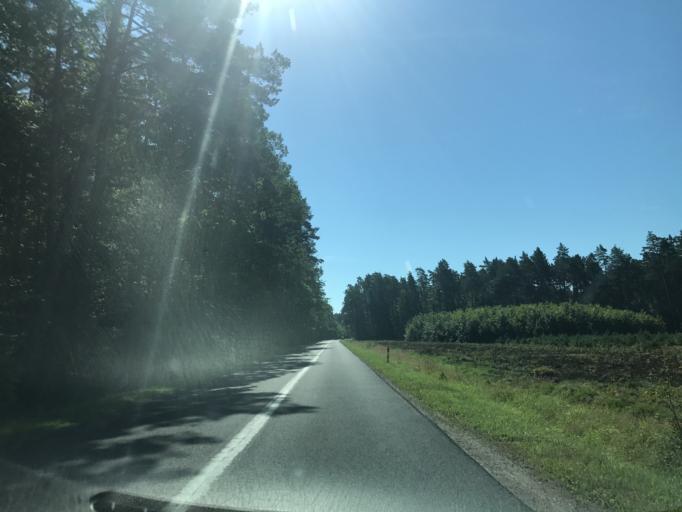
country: PL
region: Pomeranian Voivodeship
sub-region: Powiat slupski
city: Potegowo
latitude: 54.4018
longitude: 17.4570
